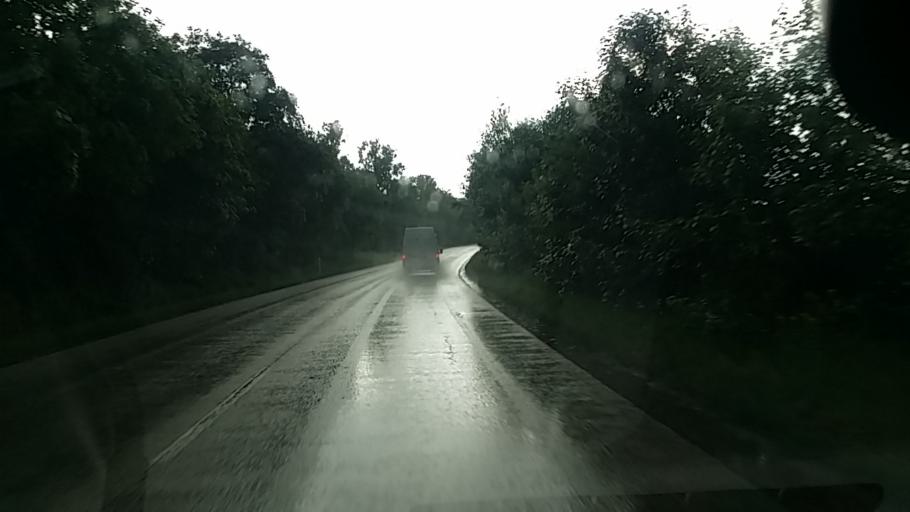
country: HU
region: Fejer
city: Etyek
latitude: 47.4956
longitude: 18.7614
